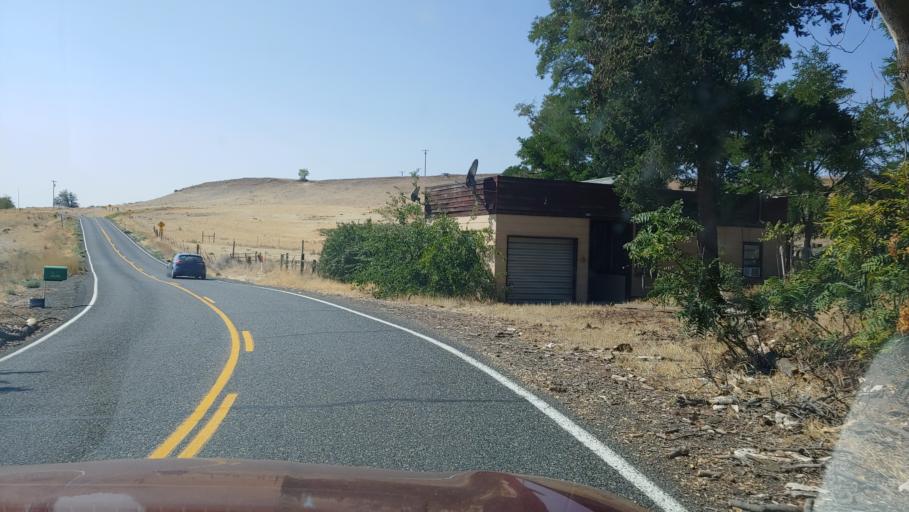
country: US
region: Washington
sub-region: Klickitat County
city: Goldendale
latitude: 45.6987
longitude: -120.8033
